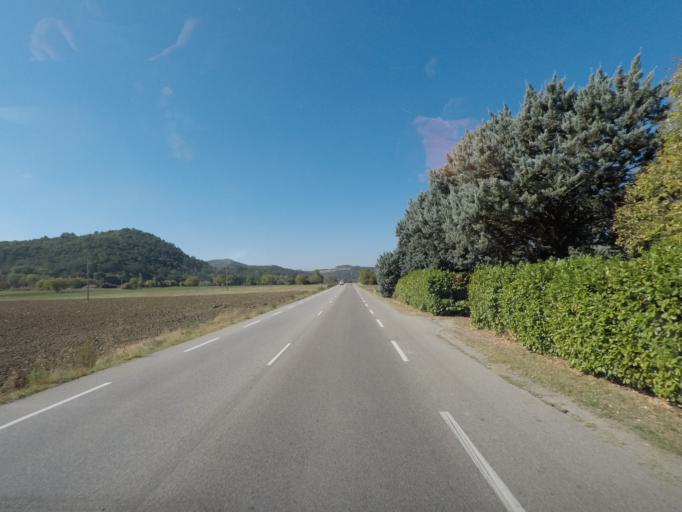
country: FR
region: Rhone-Alpes
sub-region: Departement de la Drome
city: Aouste-sur-Sye
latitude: 44.7089
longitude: 5.0733
